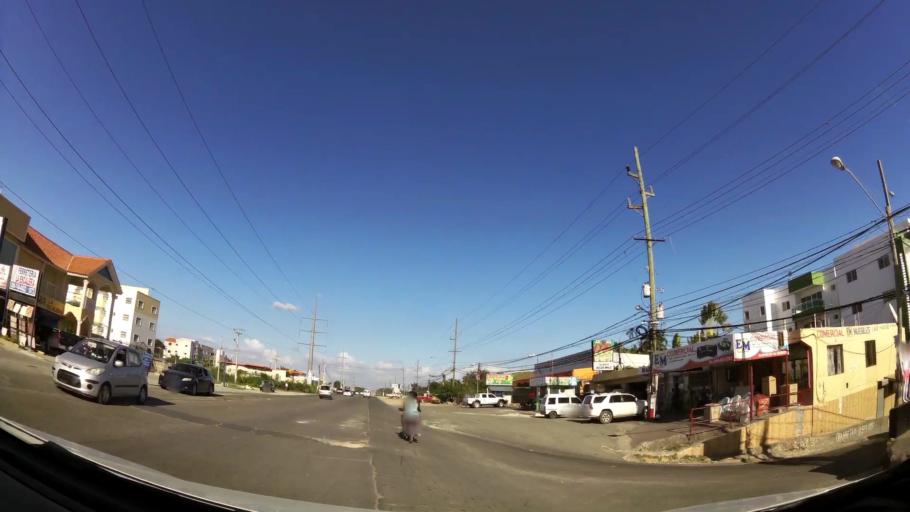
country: DO
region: Santo Domingo
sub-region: Santo Domingo
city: Santo Domingo Este
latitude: 18.4942
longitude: -69.8069
